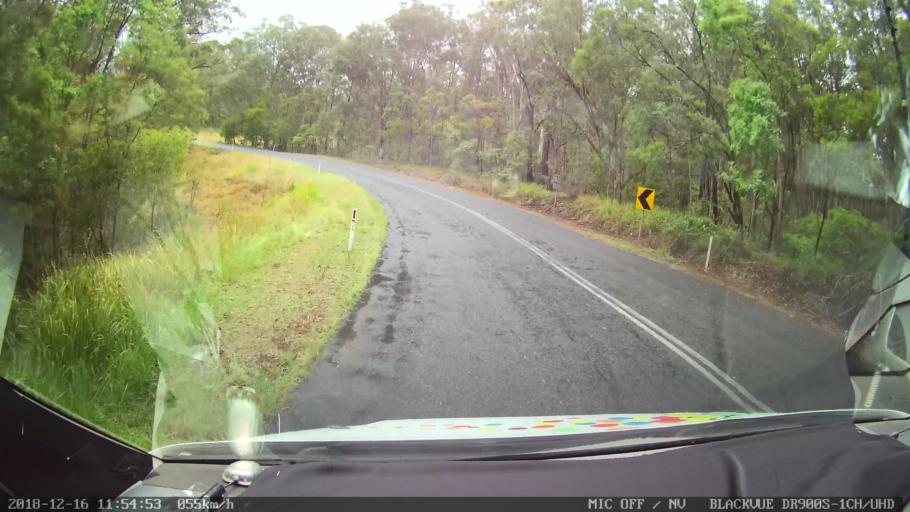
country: AU
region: New South Wales
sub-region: Tenterfield Municipality
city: Carrolls Creek
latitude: -28.9115
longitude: 152.2875
